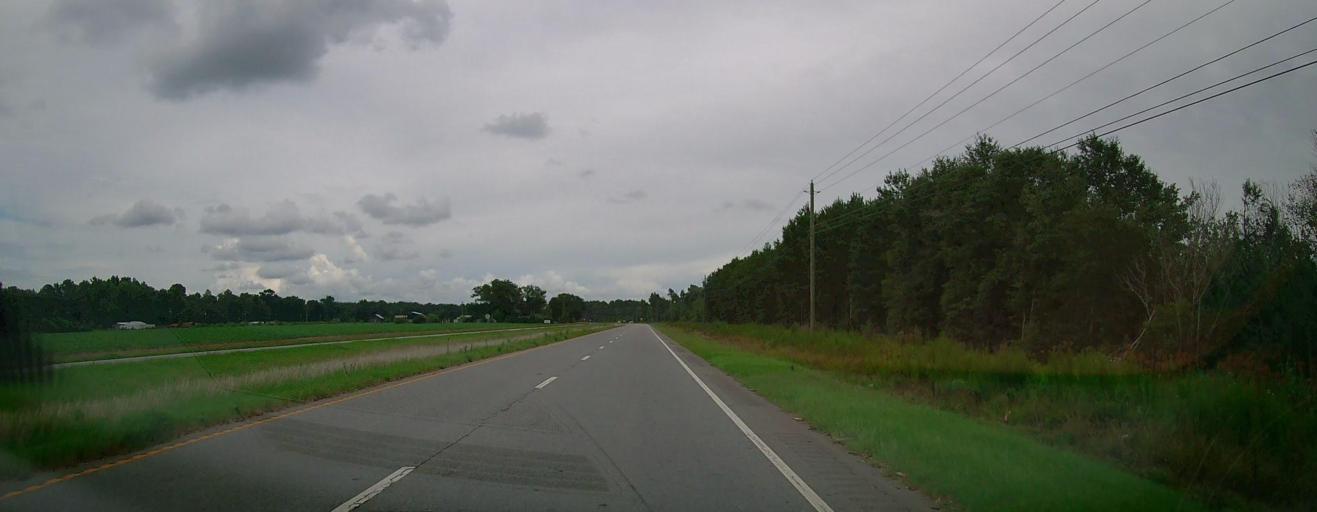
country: US
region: Georgia
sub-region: Appling County
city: Baxley
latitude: 31.7971
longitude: -82.4032
